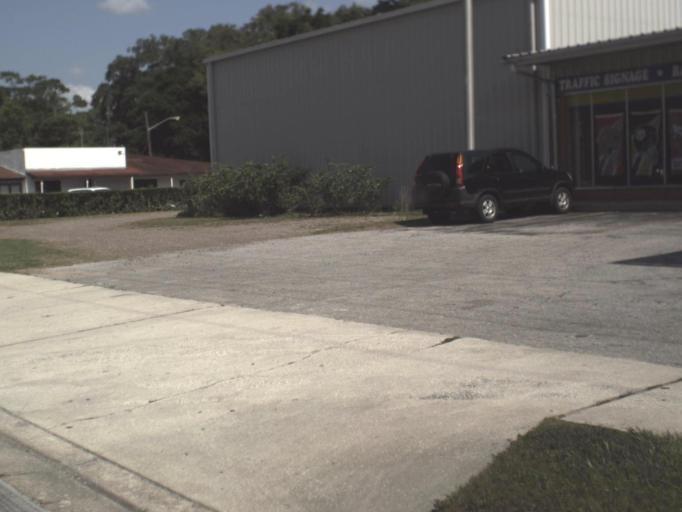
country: US
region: Florida
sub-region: Duval County
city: Jacksonville
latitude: 30.2900
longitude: -81.5903
